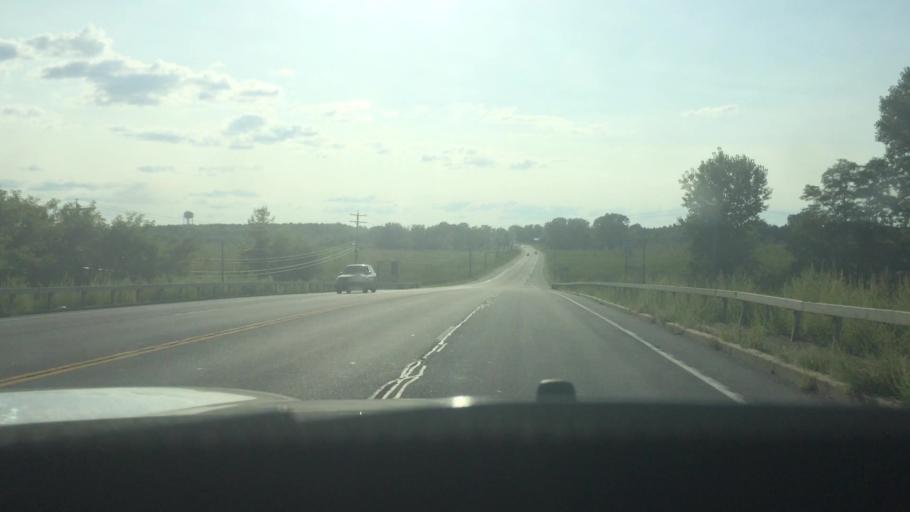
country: US
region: New York
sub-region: St. Lawrence County
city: Potsdam
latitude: 44.6674
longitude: -75.0098
